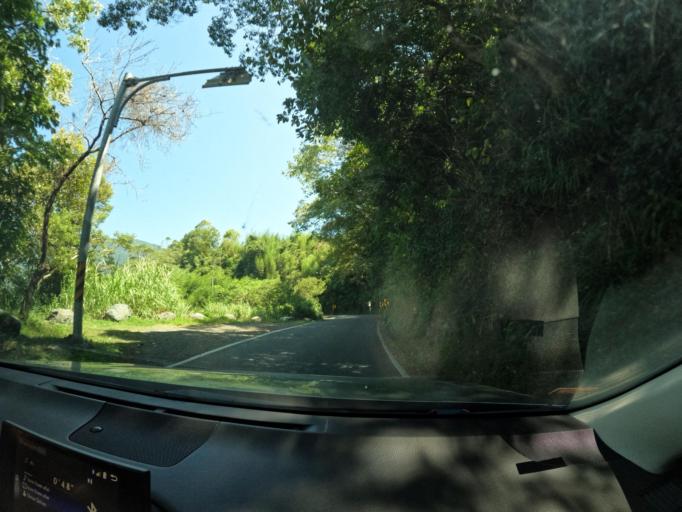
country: TW
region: Taiwan
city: Yujing
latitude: 23.2846
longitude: 120.8407
